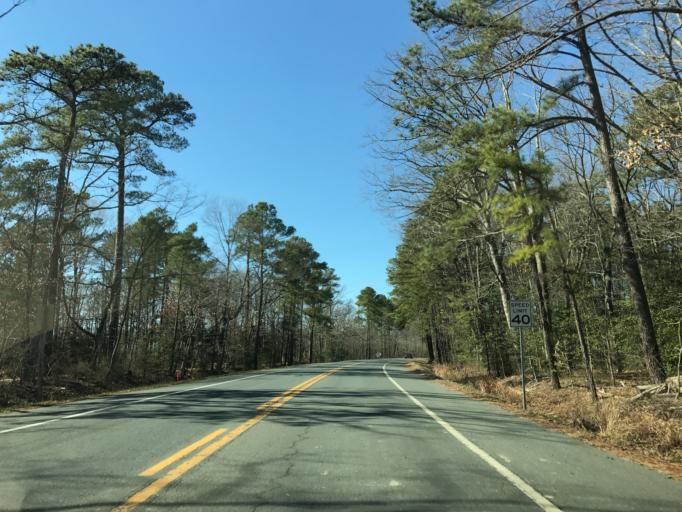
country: US
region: Maryland
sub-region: Queen Anne's County
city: Stevensville
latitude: 38.8828
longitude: -76.3433
